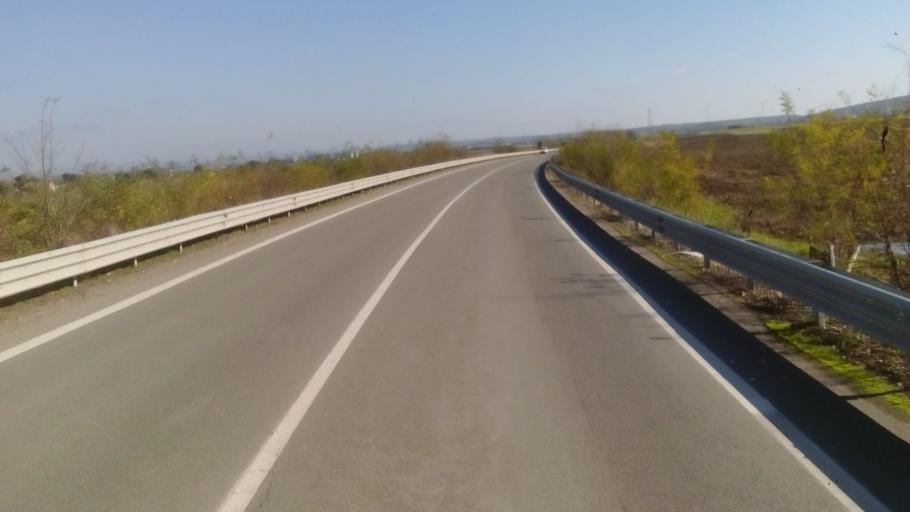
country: IT
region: Basilicate
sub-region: Provincia di Potenza
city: Zona 179
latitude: 41.0822
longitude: 15.6235
